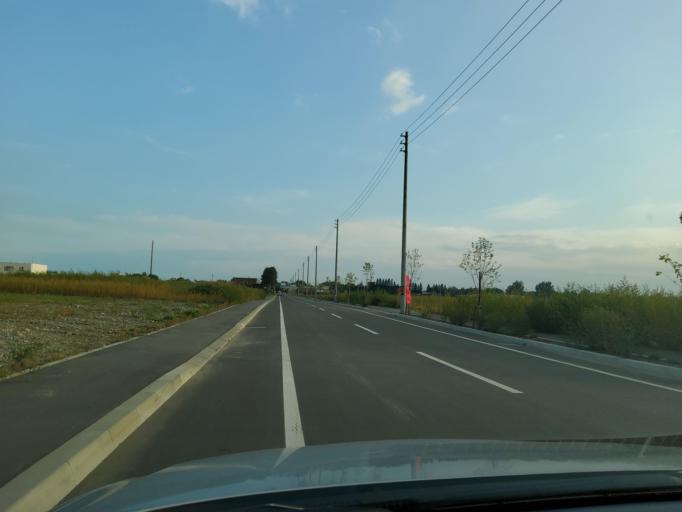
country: JP
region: Hokkaido
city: Obihiro
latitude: 42.9382
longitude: 143.1531
